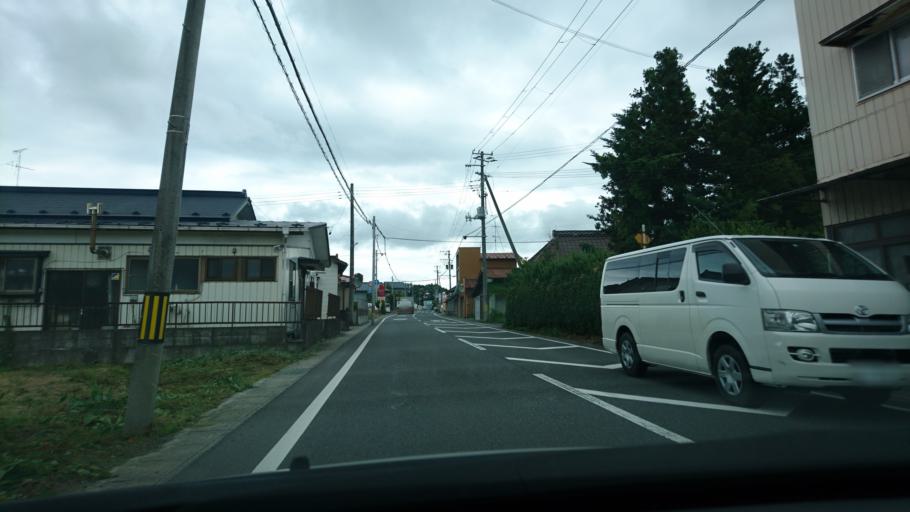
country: JP
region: Miyagi
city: Wakuya
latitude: 38.7295
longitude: 141.2600
